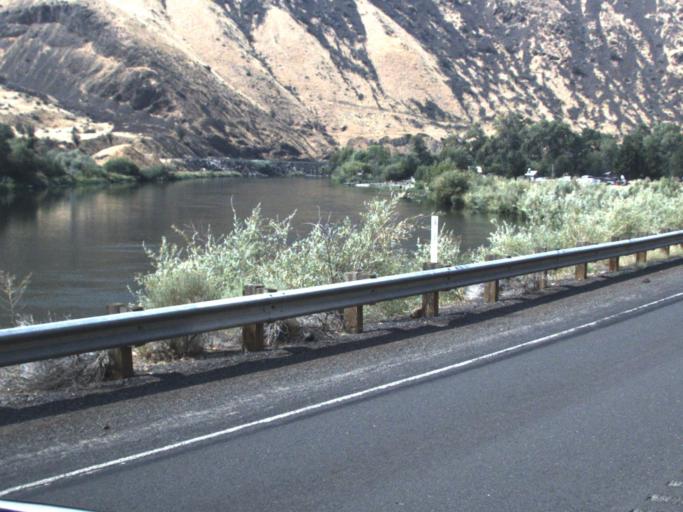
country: US
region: Washington
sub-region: Yakima County
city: Selah
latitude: 46.7624
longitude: -120.4532
